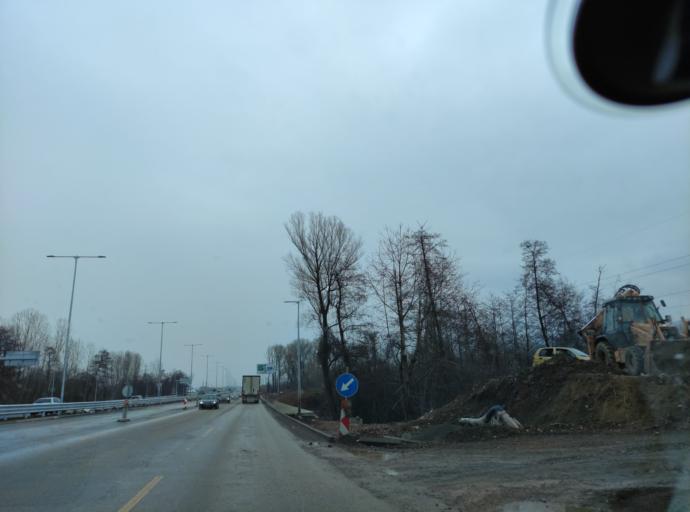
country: BG
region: Sofia-Capital
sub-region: Stolichna Obshtina
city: Sofia
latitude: 42.6221
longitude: 23.4102
